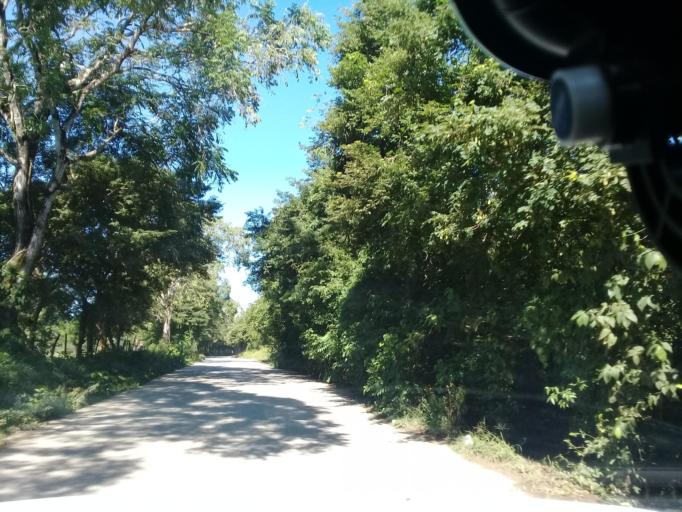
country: MX
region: Hidalgo
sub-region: Huejutla de Reyes
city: Huejutla de Reyes
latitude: 21.1655
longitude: -98.4200
